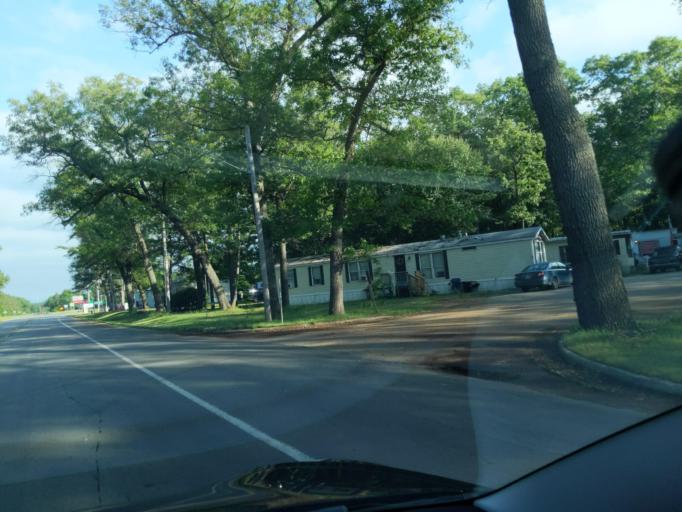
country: US
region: Michigan
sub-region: Muskegon County
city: Lakewood Club
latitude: 43.3933
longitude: -86.2993
